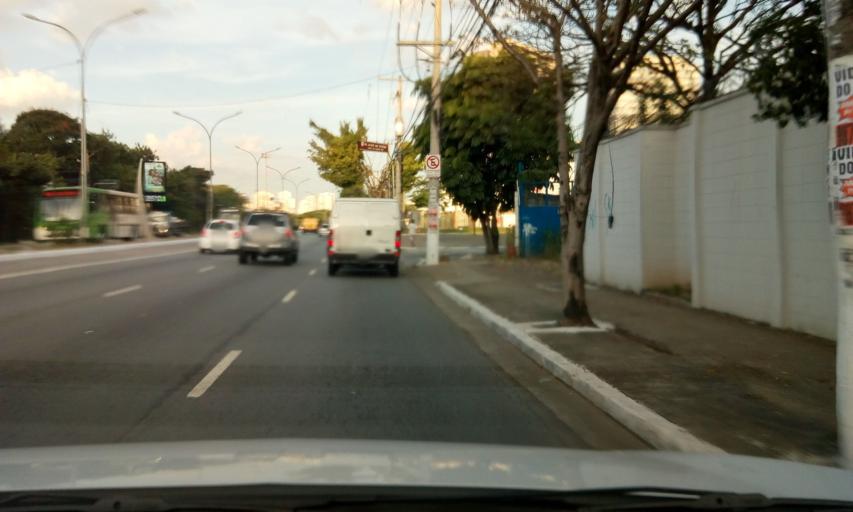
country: BR
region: Sao Paulo
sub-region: Sao Paulo
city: Sao Paulo
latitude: -23.5170
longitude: -46.6836
